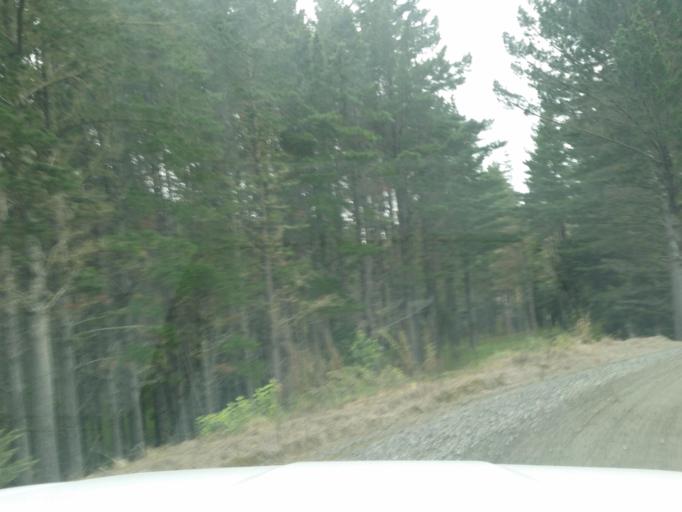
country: NZ
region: Northland
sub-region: Kaipara District
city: Dargaville
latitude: -35.7961
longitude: 173.9874
